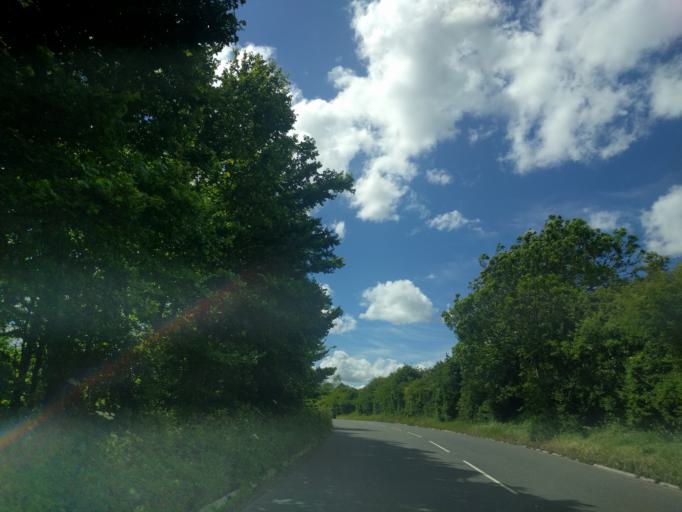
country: GB
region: England
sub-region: Wiltshire
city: Fyfield
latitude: 51.4188
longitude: -1.7798
